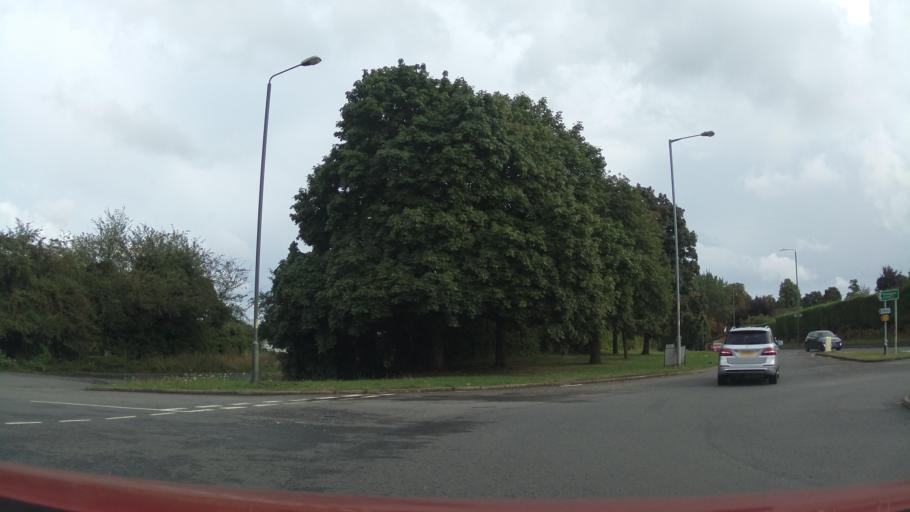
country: GB
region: England
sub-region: Worcestershire
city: Kidderminster
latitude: 52.3778
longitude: -2.2264
